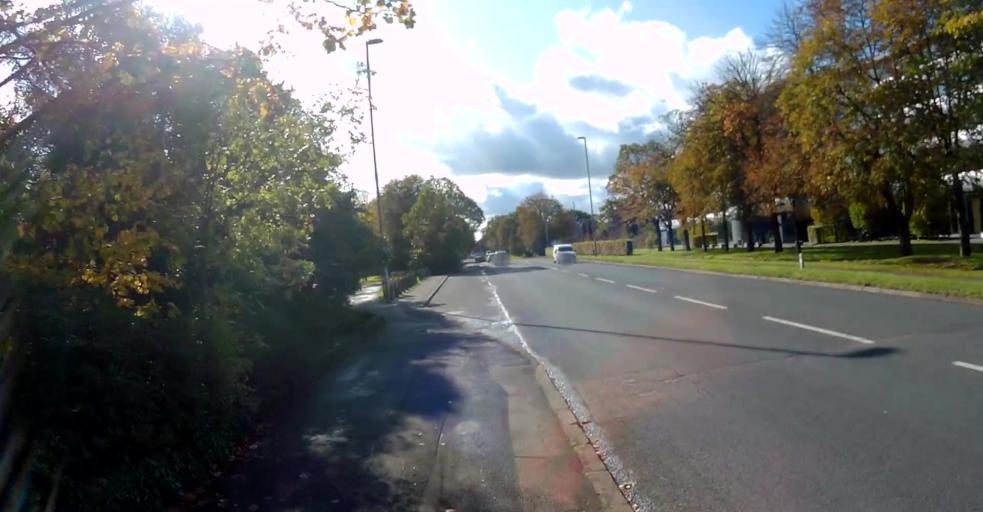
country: GB
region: England
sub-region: Hampshire
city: Farnborough
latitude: 51.2798
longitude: -0.7539
